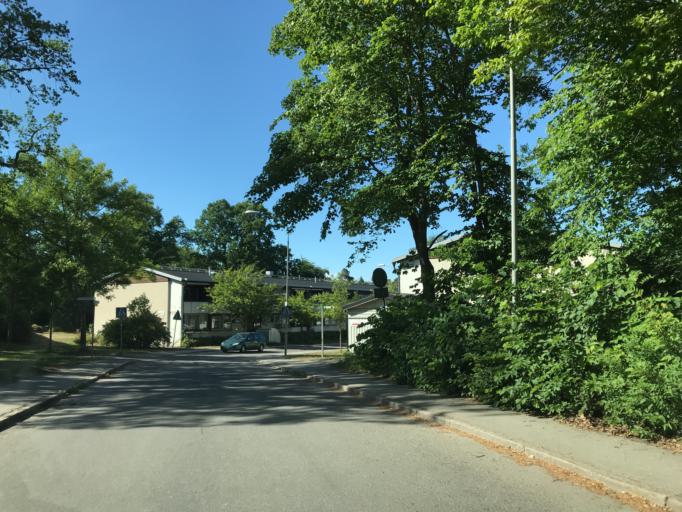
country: SE
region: Stockholm
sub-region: Huddinge Kommun
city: Segeltorp
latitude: 59.2988
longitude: 17.9386
